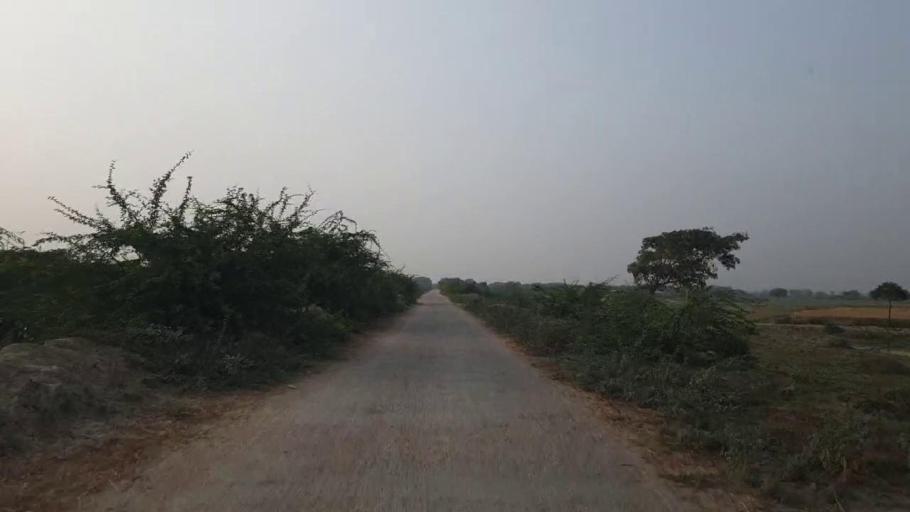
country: PK
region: Sindh
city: Mirpur Batoro
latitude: 24.6482
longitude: 68.3912
